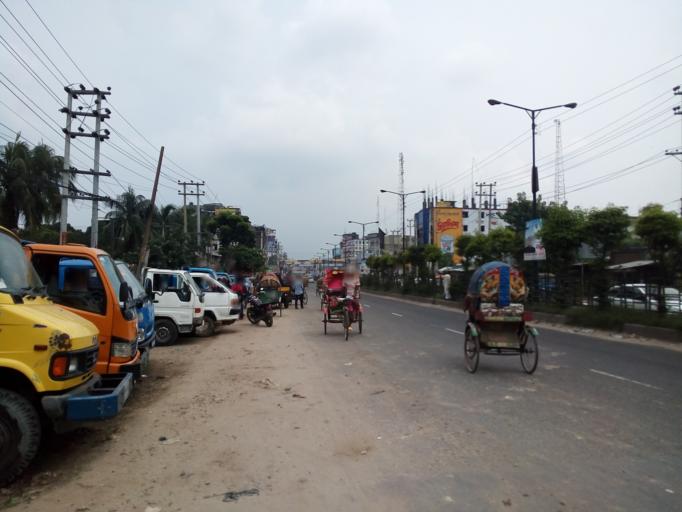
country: BD
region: Dhaka
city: Tungi
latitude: 23.8455
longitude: 90.2565
